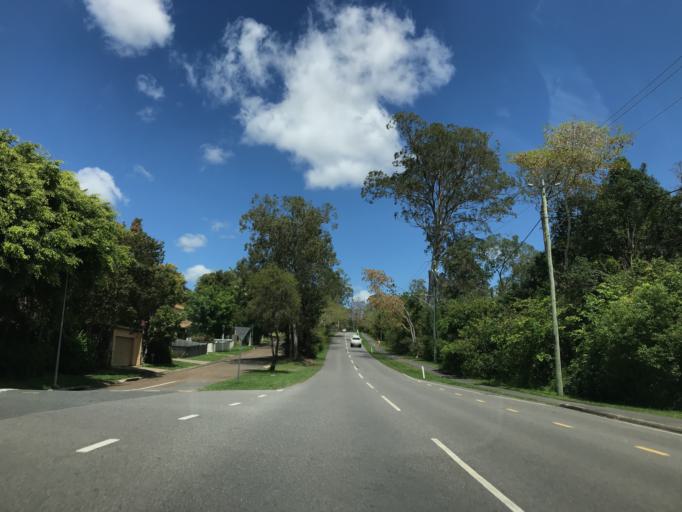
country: AU
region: Queensland
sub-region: Moreton Bay
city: Ferny Hills
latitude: -27.4500
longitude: 152.9421
